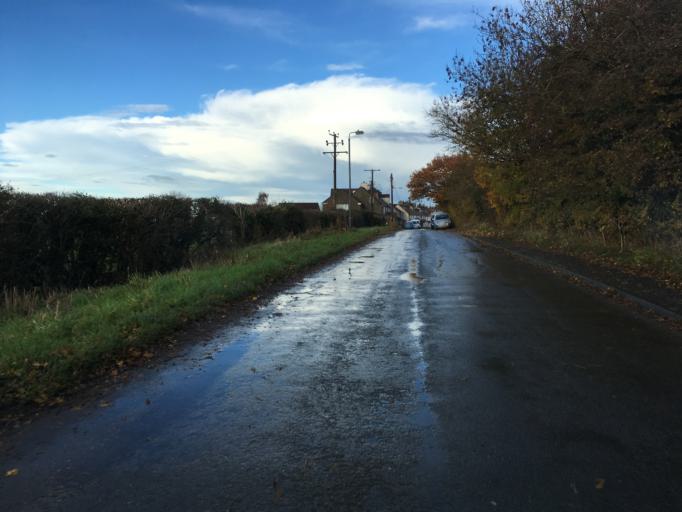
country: GB
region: England
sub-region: South Gloucestershire
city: Pucklechurch
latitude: 51.4925
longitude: -2.4472
